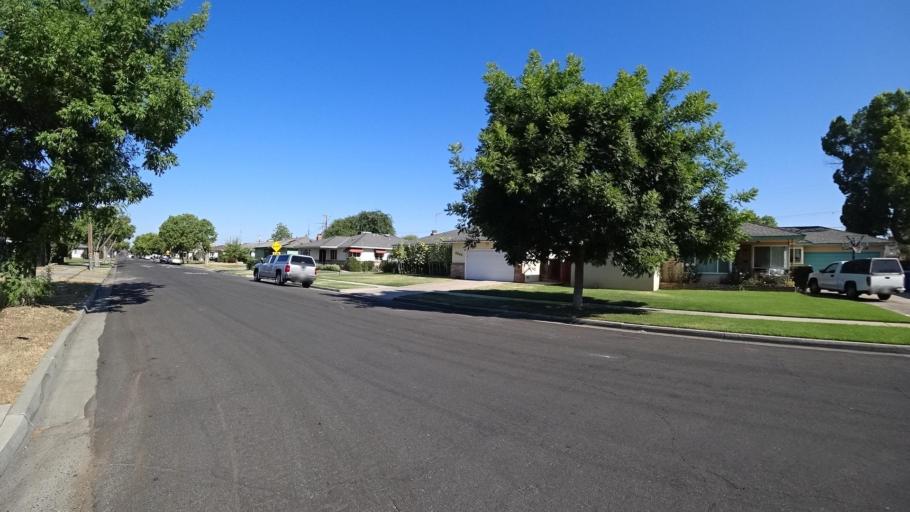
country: US
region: California
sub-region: Fresno County
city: Fresno
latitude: 36.7823
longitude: -119.7646
